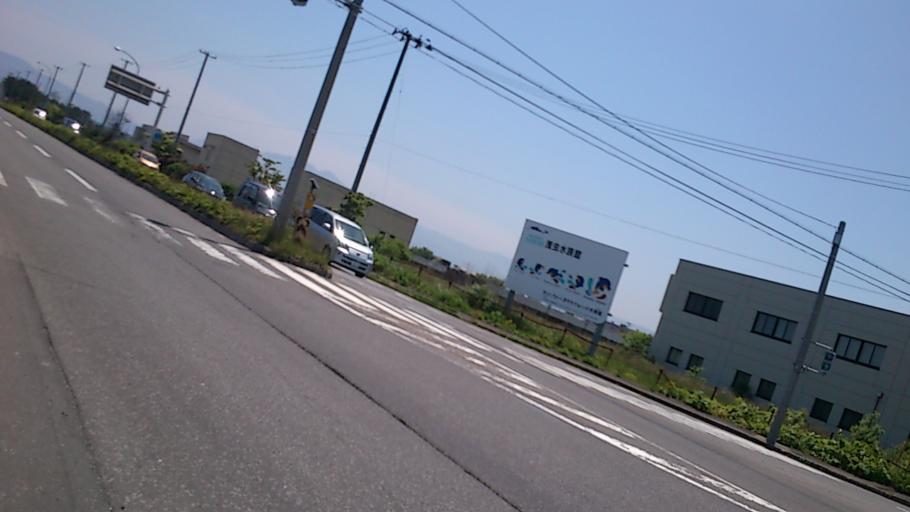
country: JP
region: Aomori
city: Aomori Shi
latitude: 40.8445
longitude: 140.7147
